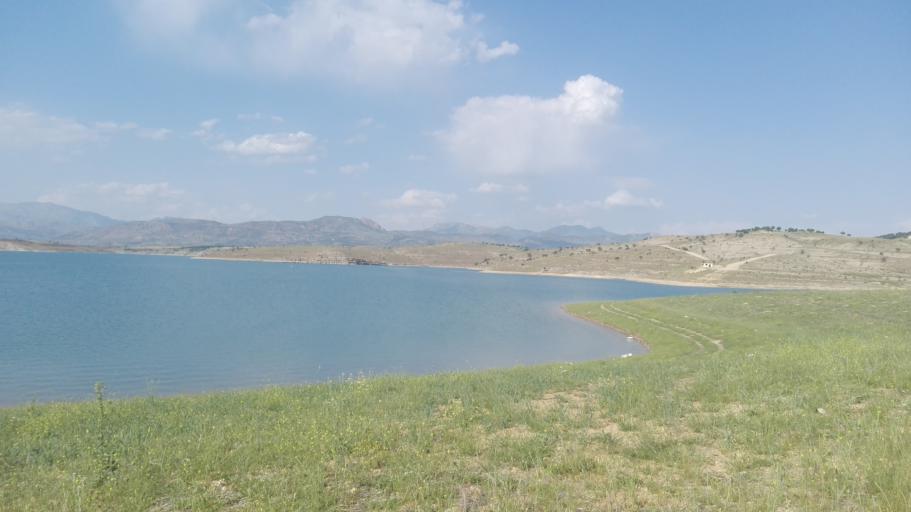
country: TR
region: Diyarbakir
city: Malabadi
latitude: 38.1819
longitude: 41.2175
